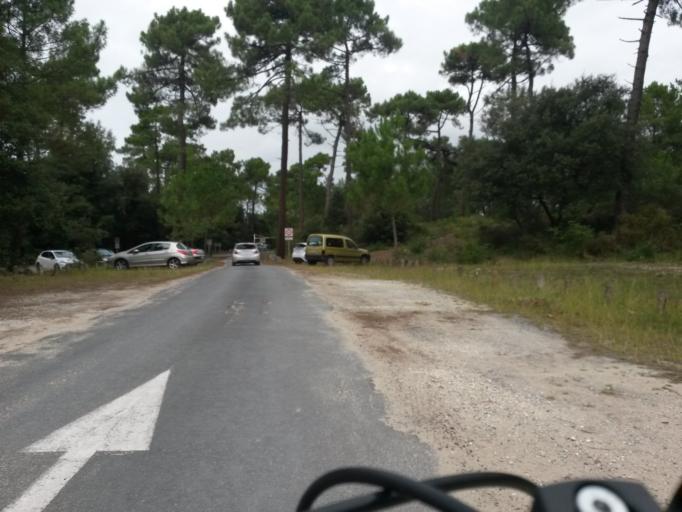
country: FR
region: Poitou-Charentes
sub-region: Departement de la Charente-Maritime
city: Saint-Trojan-les-Bains
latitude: 45.8147
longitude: -1.2194
